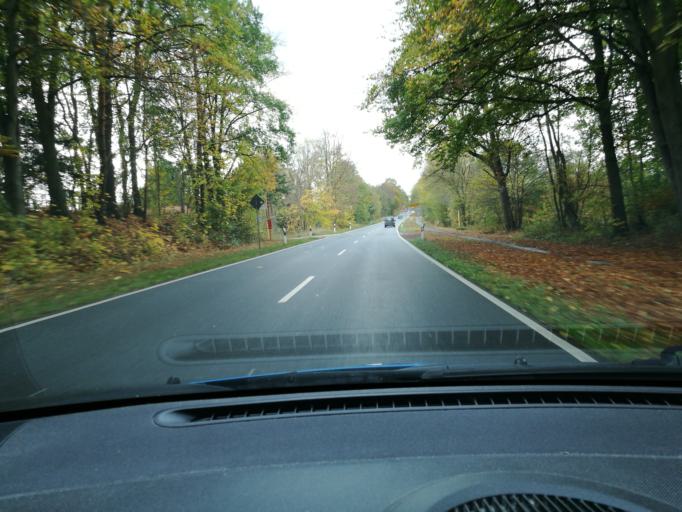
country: DE
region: Schleswig-Holstein
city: Gross Sarau
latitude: 53.7783
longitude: 10.7474
